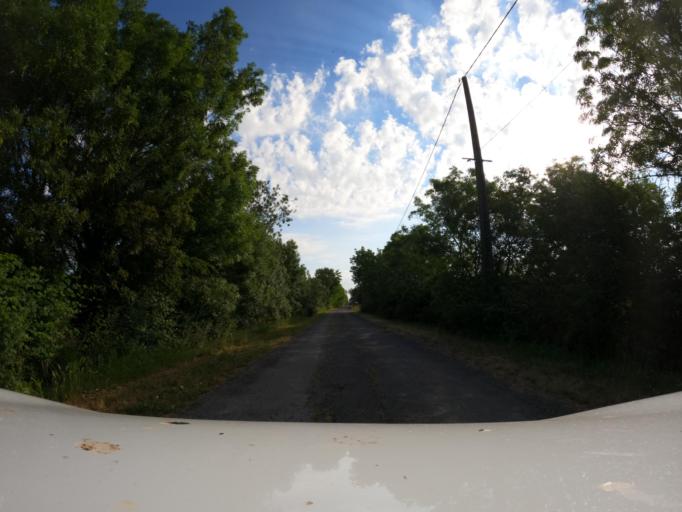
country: FR
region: Pays de la Loire
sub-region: Departement de la Vendee
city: Champagne-les-Marais
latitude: 46.3641
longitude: -1.0825
